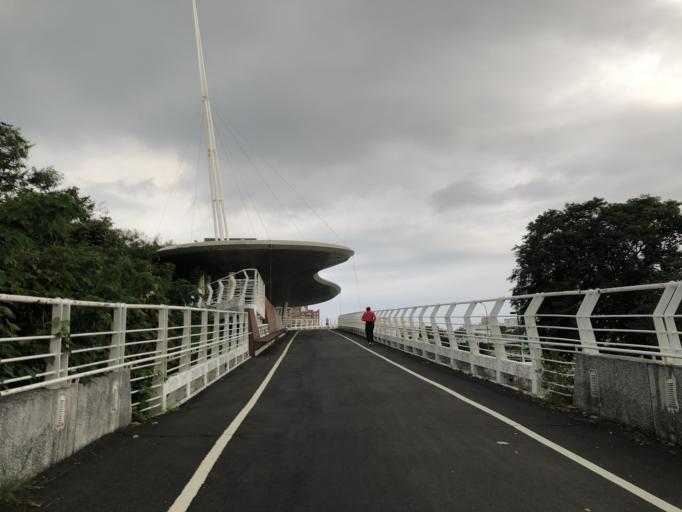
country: TW
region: Kaohsiung
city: Kaohsiung
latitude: 22.6804
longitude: 120.2981
